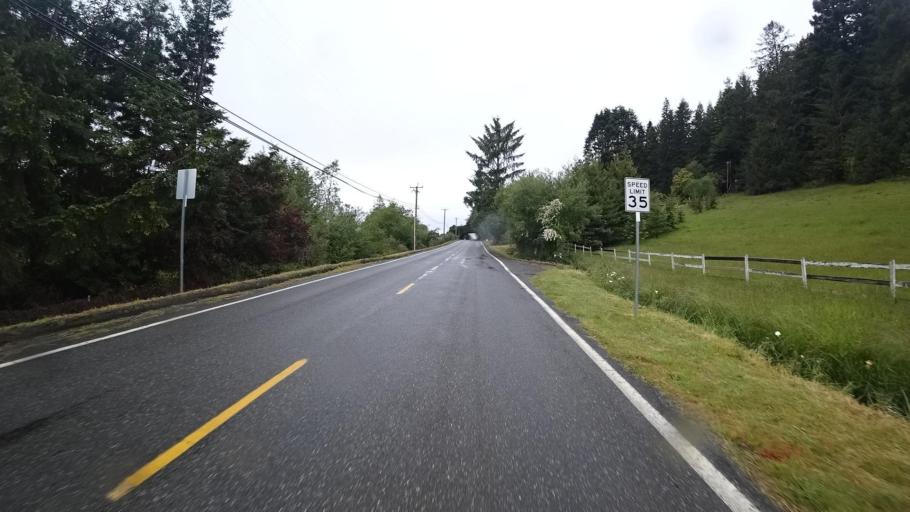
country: US
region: California
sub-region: Humboldt County
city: Bayside
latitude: 40.8373
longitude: -124.0528
